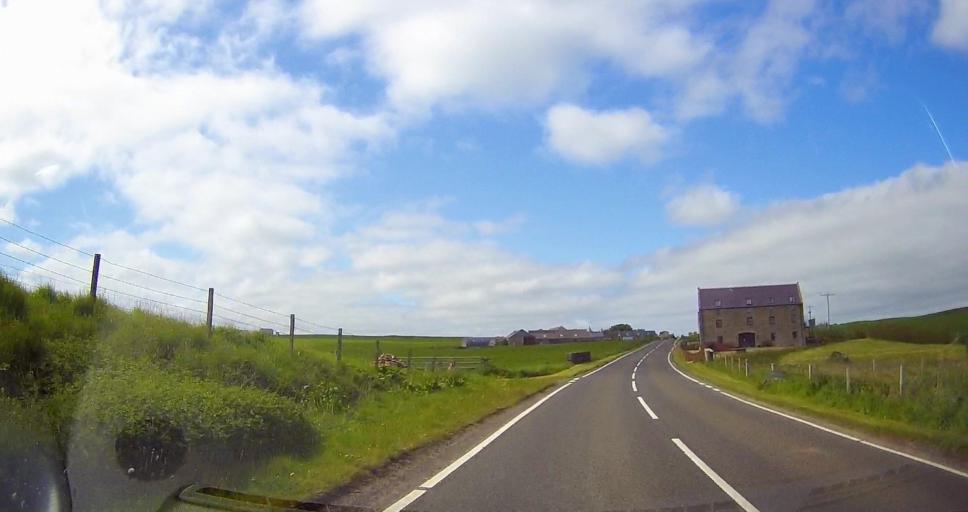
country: GB
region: Scotland
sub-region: Orkney Islands
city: Kirkwall
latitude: 58.9257
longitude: -2.8422
